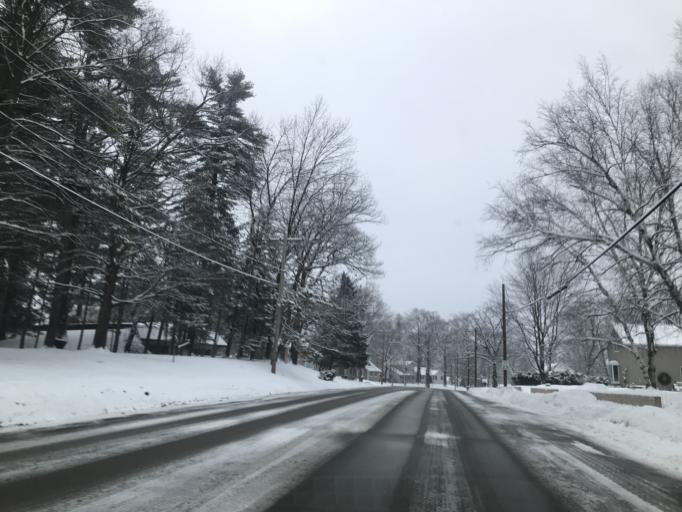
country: US
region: Wisconsin
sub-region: Oconto County
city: Oconto Falls
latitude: 44.8697
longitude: -88.1346
